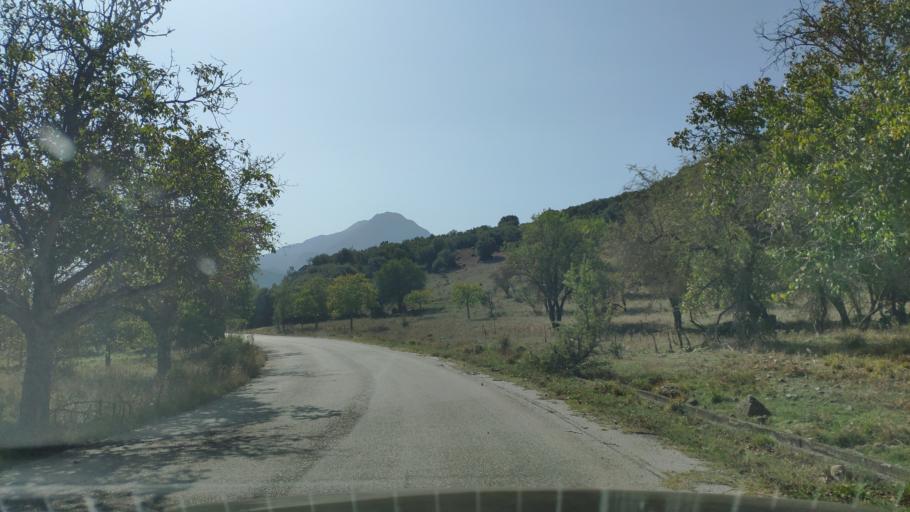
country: GR
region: West Greece
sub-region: Nomos Achaias
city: Aiyira
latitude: 37.9591
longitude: 22.3443
